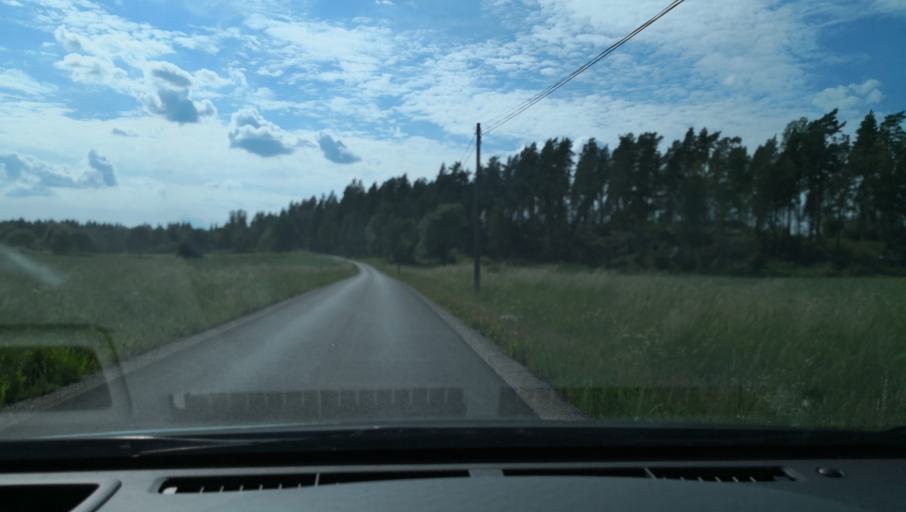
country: SE
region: Uppsala
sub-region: Enkopings Kommun
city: Orsundsbro
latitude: 59.8408
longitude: 17.2858
